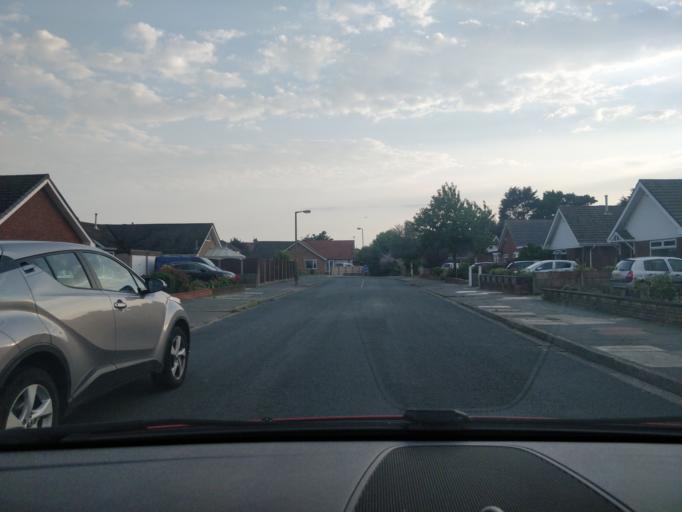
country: GB
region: England
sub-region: Sefton
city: Southport
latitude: 53.6718
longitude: -2.9716
